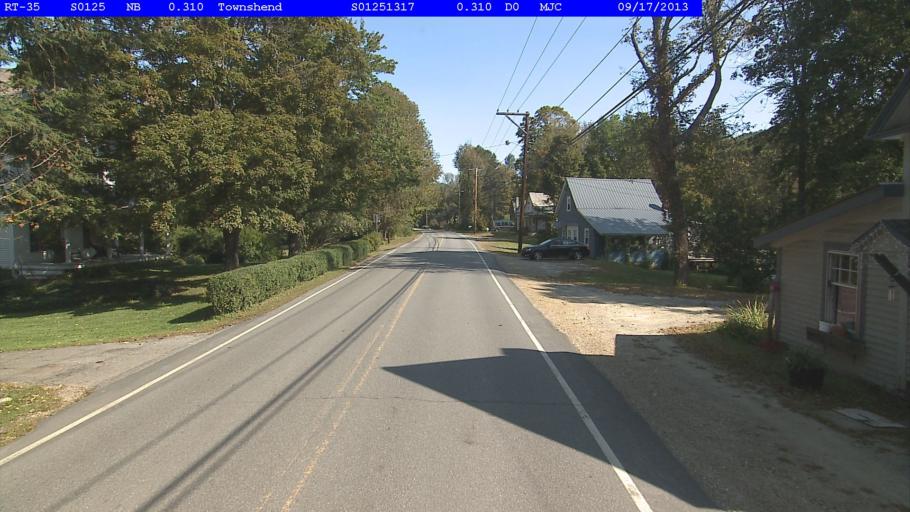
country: US
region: Vermont
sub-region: Windham County
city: Newfane
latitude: 43.0504
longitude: -72.6668
